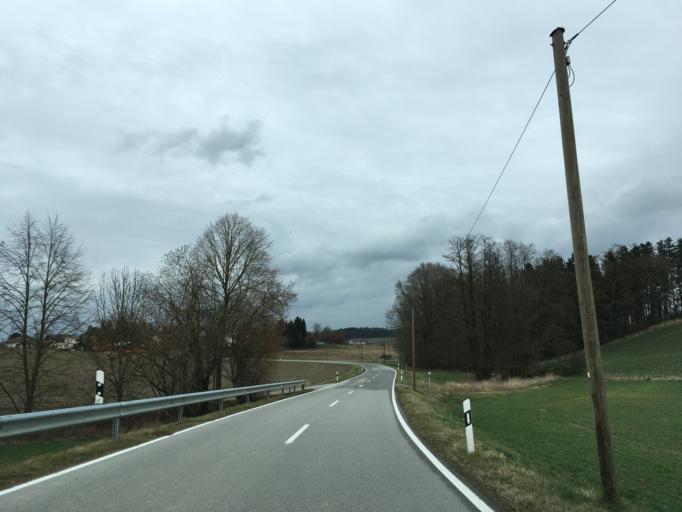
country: DE
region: Bavaria
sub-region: Upper Bavaria
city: Oberbergkirchen
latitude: 48.2740
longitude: 12.3529
